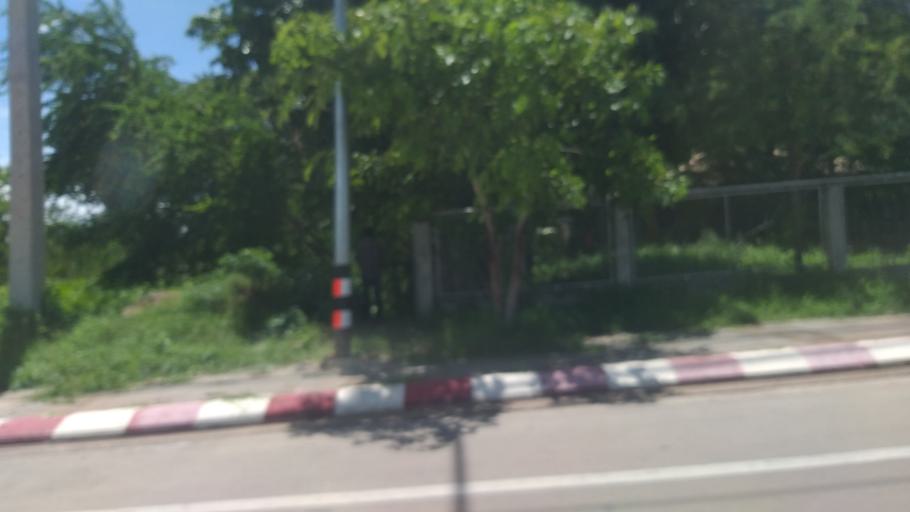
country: TH
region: Khon Kaen
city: Khon Kaen
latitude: 16.4339
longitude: 102.8194
